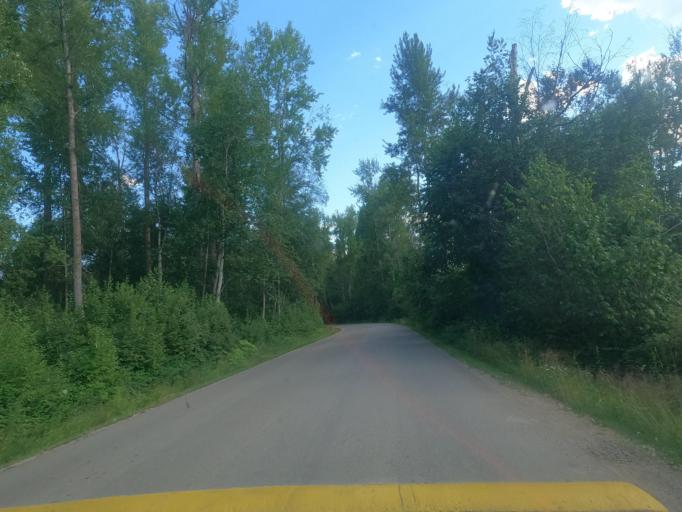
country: CA
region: British Columbia
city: Salmon Arm
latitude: 50.7326
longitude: -119.3145
